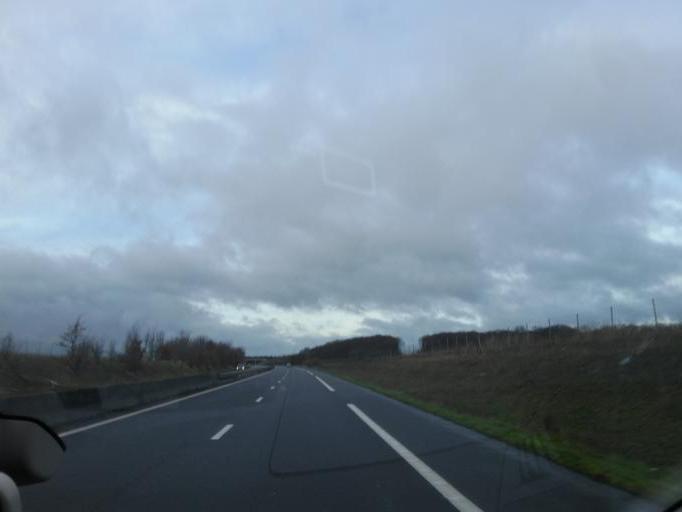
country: FR
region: Picardie
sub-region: Departement de la Somme
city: Villers-Bretonneux
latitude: 49.8571
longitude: 2.4935
